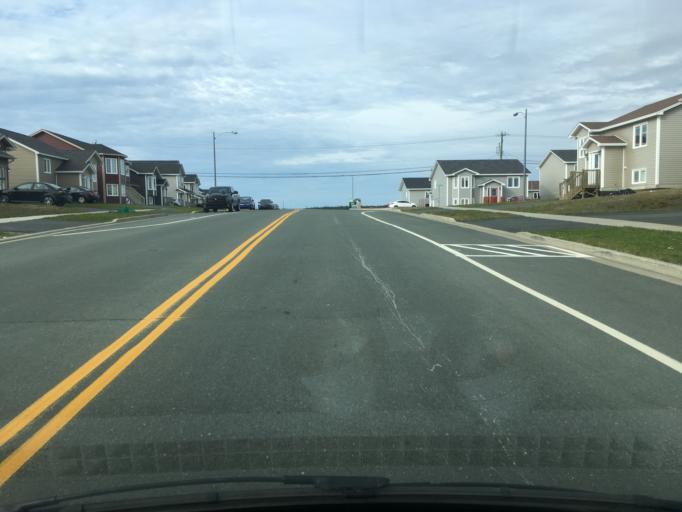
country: CA
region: Newfoundland and Labrador
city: Mount Pearl
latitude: 47.5504
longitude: -52.7889
